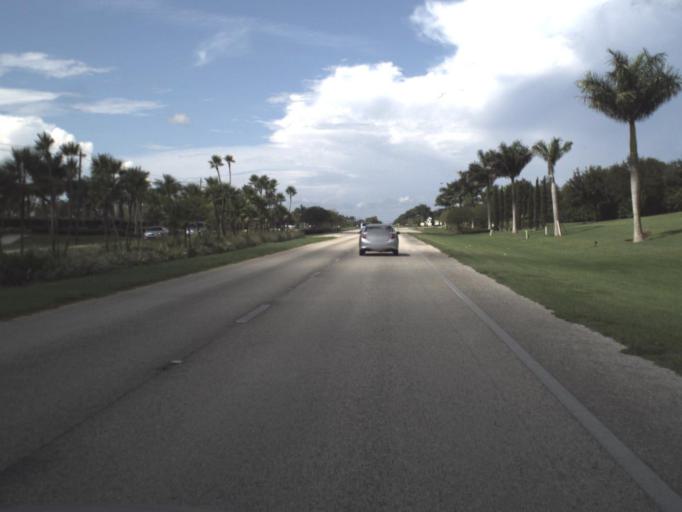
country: US
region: Florida
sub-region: Sarasota County
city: Plantation
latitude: 27.0497
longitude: -82.3395
